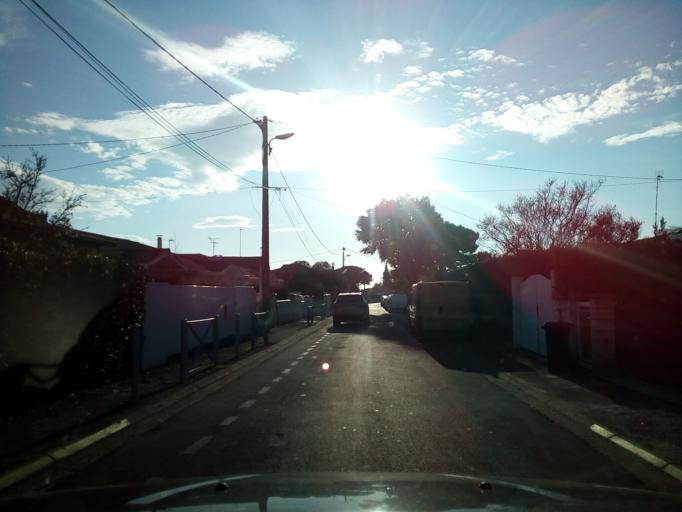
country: FR
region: Aquitaine
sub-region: Departement de la Gironde
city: Andernos-les-Bains
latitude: 44.7445
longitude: -1.1028
